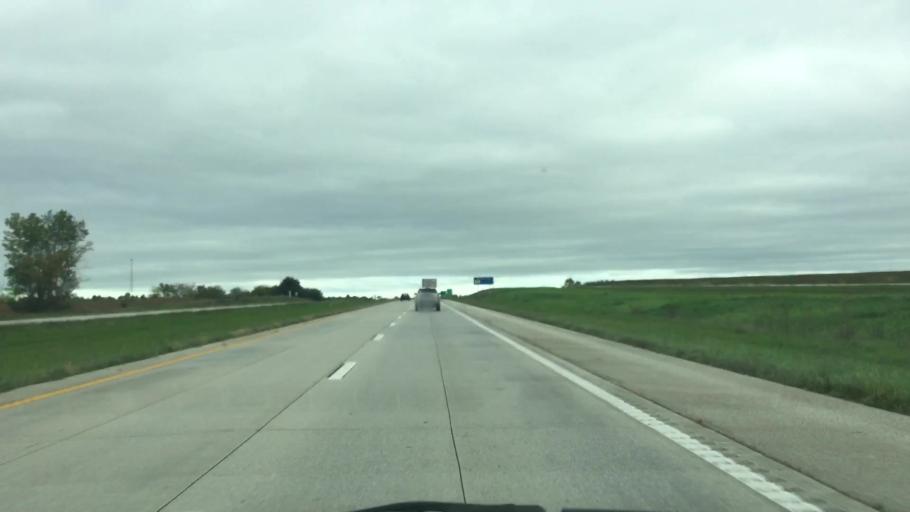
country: US
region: Missouri
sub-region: Daviess County
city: Gallatin
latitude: 40.0682
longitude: -94.0936
